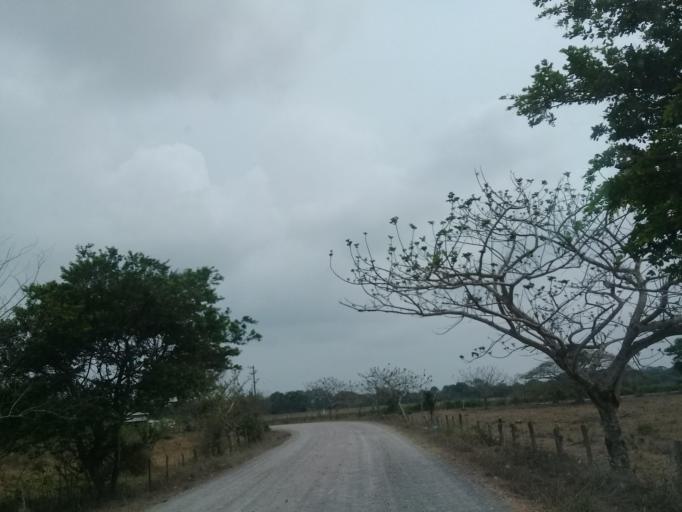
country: MX
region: Veracruz
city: El Tejar
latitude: 19.0604
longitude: -96.1980
